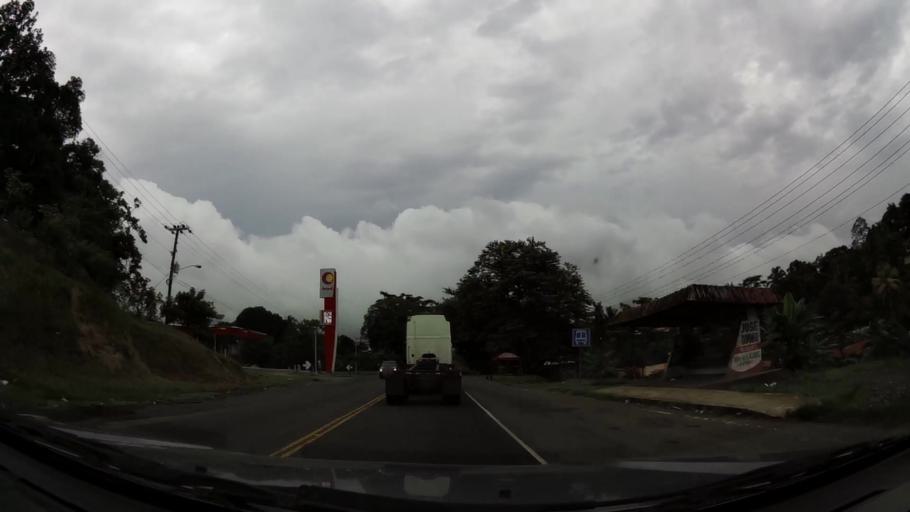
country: PA
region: Colon
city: Nuevo Vigia
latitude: 9.2295
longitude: -79.6289
